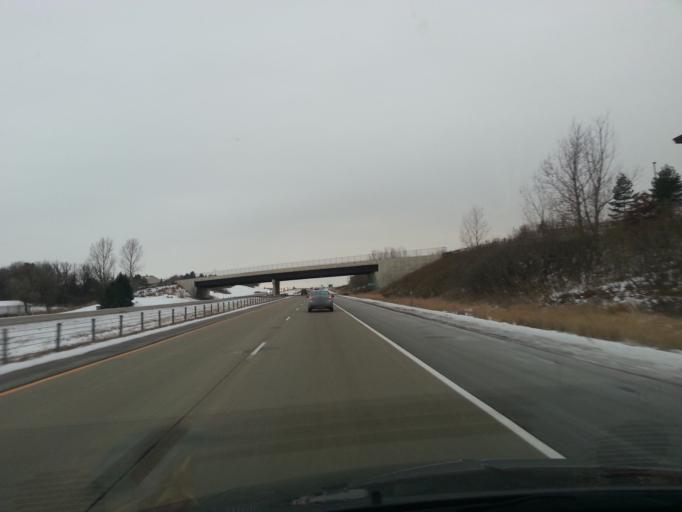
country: US
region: Minnesota
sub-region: Dakota County
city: Burnsville
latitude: 44.7507
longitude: -93.2663
